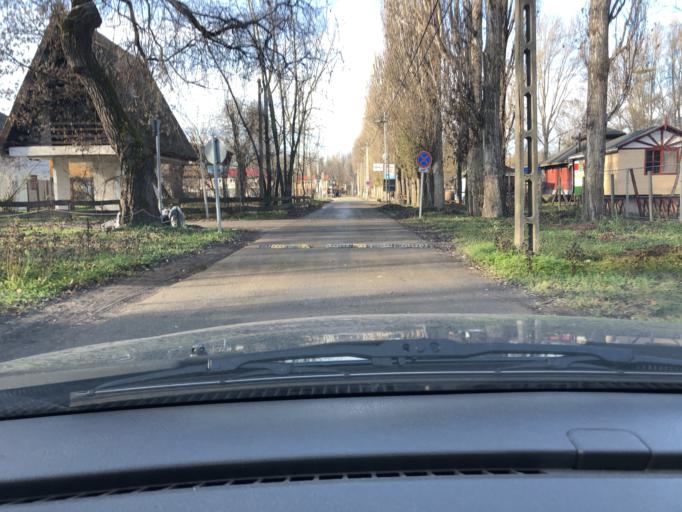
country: HU
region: Csongrad
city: Csongrad
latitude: 46.7147
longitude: 20.1861
